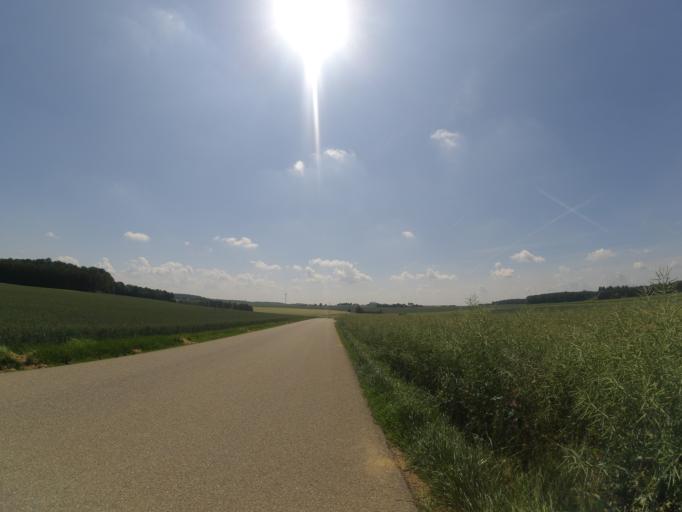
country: DE
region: Baden-Wuerttemberg
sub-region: Tuebingen Region
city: Bernstadt
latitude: 48.4677
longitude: 10.0197
